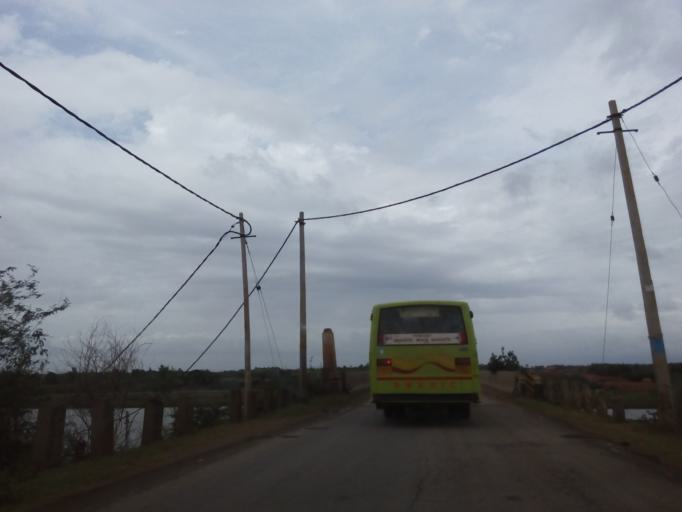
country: IN
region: Karnataka
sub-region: Davanagere
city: Harihar
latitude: 14.5157
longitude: 75.7860
